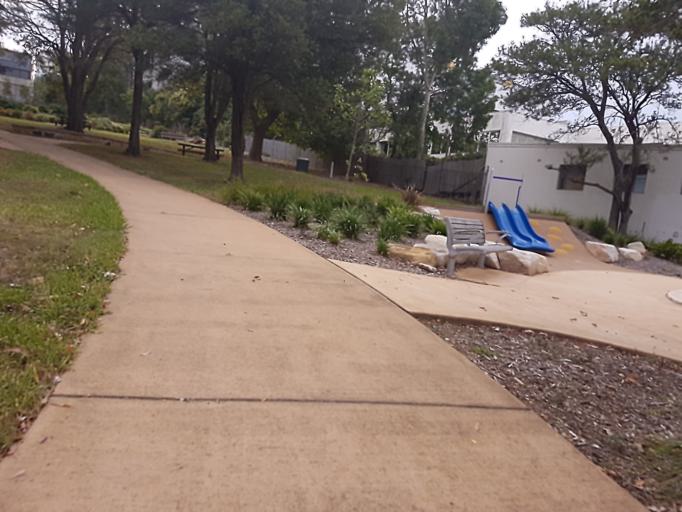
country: AU
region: New South Wales
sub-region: Willoughby
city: Castle Cove
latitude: -33.7885
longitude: 151.2020
